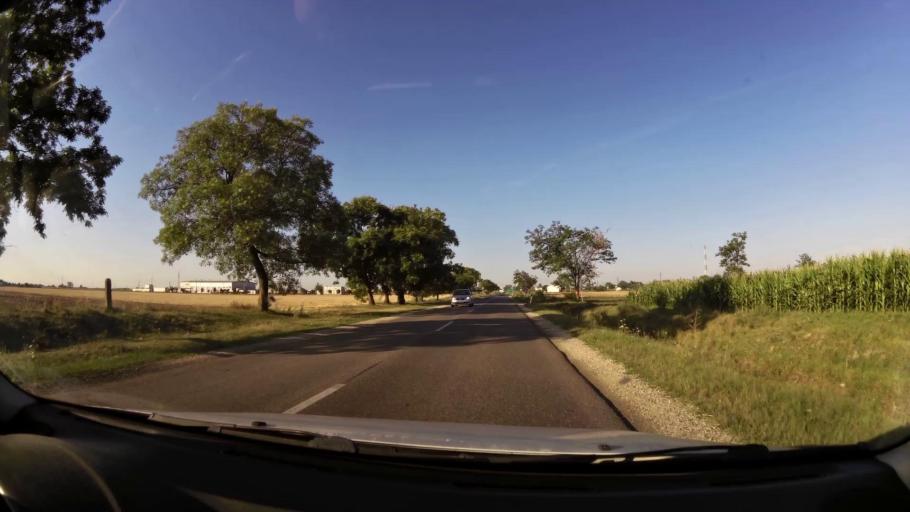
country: HU
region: Pest
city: Cegled
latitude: 47.2012
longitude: 19.8161
